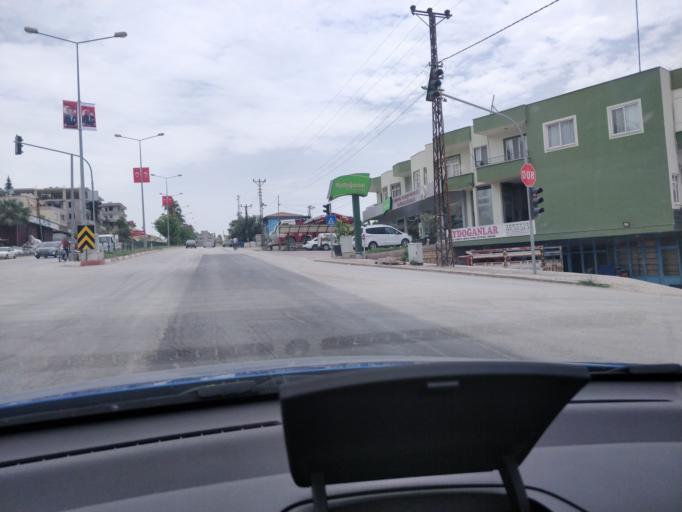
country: TR
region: Mersin
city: Mut
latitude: 36.6501
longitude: 33.4259
